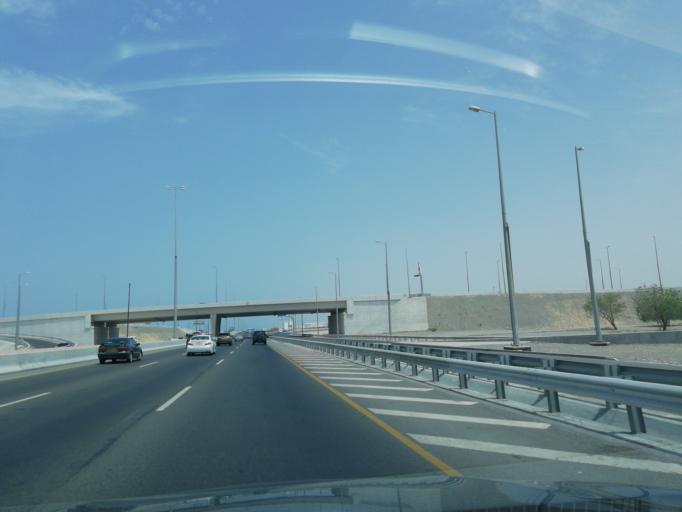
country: OM
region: Muhafazat Masqat
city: As Sib al Jadidah
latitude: 23.6593
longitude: 58.1861
